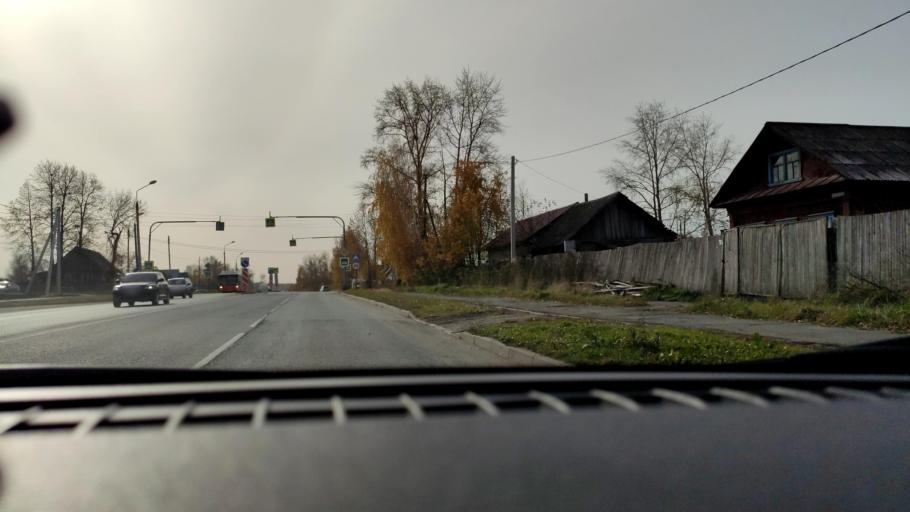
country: RU
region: Perm
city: Polazna
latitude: 58.1240
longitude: 56.4045
